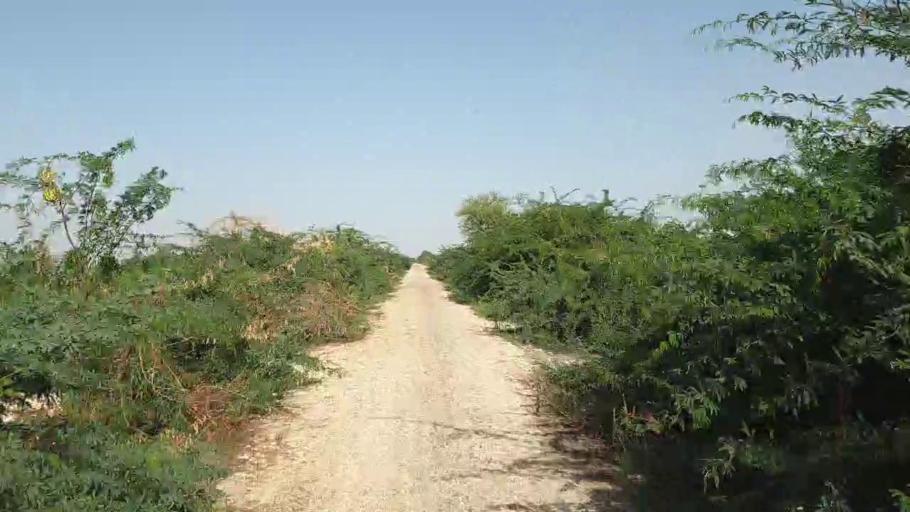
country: PK
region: Sindh
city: Tando Bago
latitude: 24.7210
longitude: 69.0731
